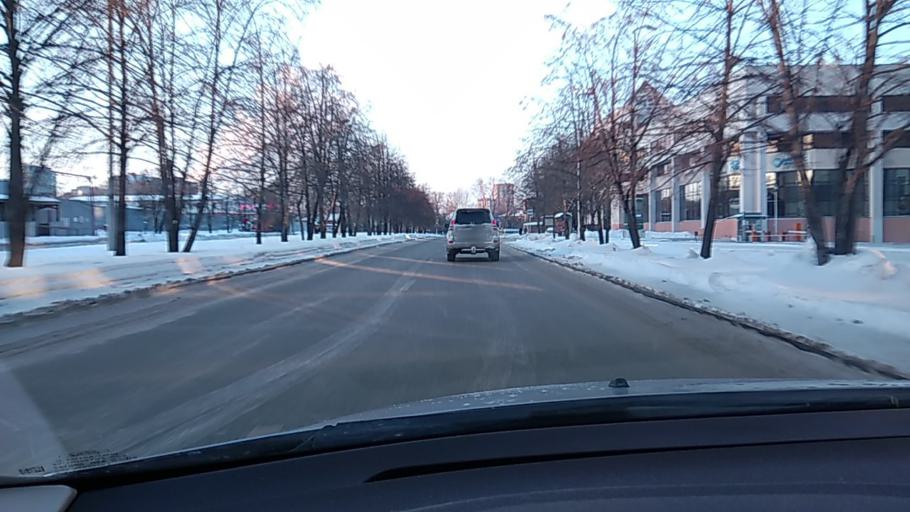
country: RU
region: Sverdlovsk
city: Yekaterinburg
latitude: 56.8446
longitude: 60.5897
